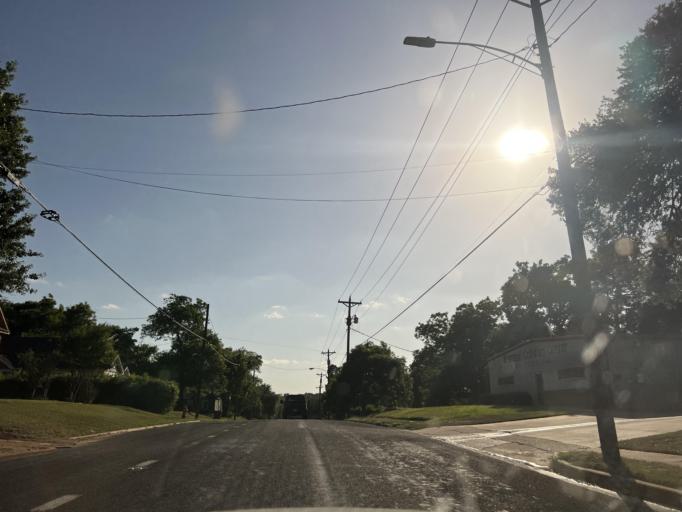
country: US
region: Texas
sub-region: Washington County
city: Brenham
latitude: 30.1654
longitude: -96.4076
